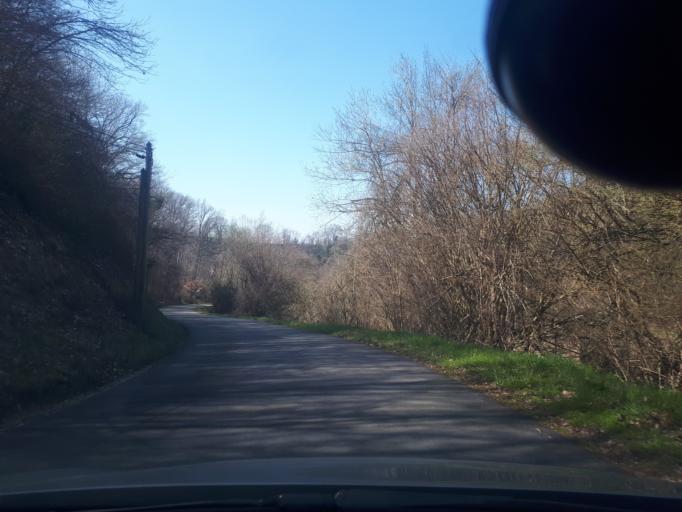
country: FR
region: Rhone-Alpes
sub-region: Departement de l'Isere
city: Nivolas-Vermelle
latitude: 45.5237
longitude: 5.3455
